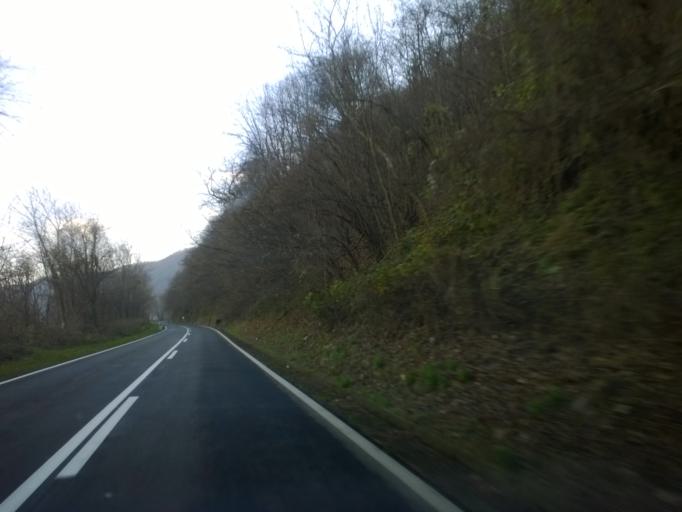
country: RS
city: Radenka
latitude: 44.6525
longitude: 21.8002
